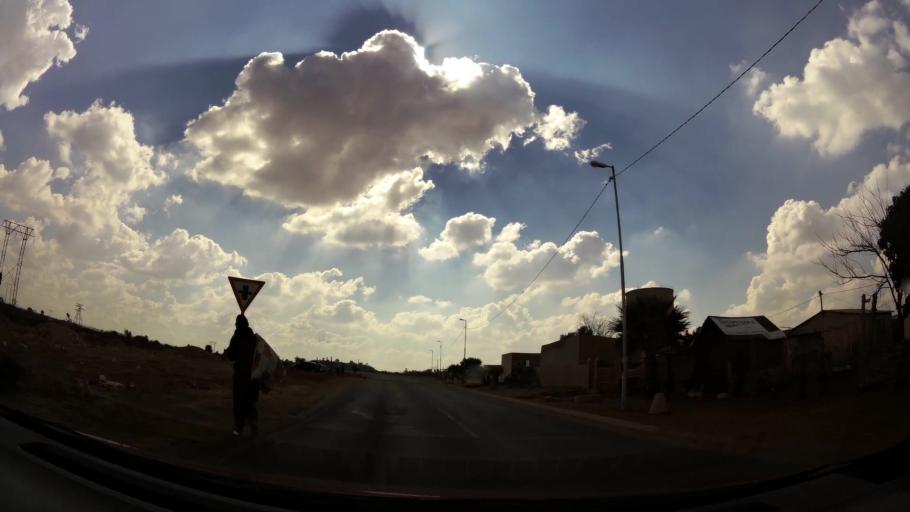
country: ZA
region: Gauteng
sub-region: City of Johannesburg Metropolitan Municipality
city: Roodepoort
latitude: -26.1876
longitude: 27.8561
